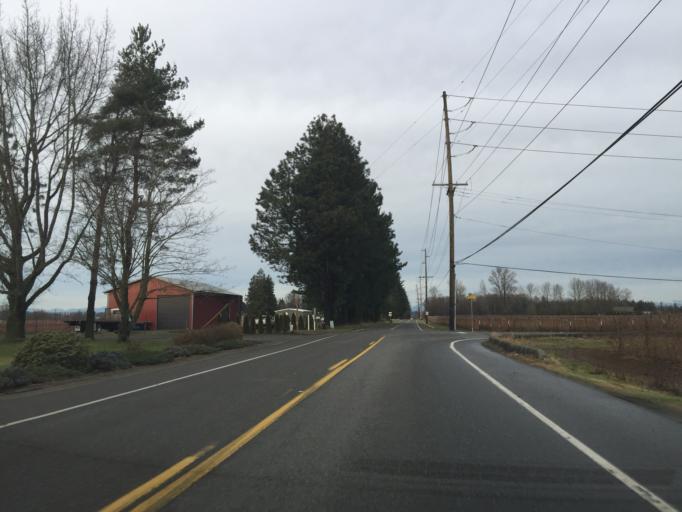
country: US
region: Washington
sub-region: Whatcom County
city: Ferndale
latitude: 48.8874
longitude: -122.5406
